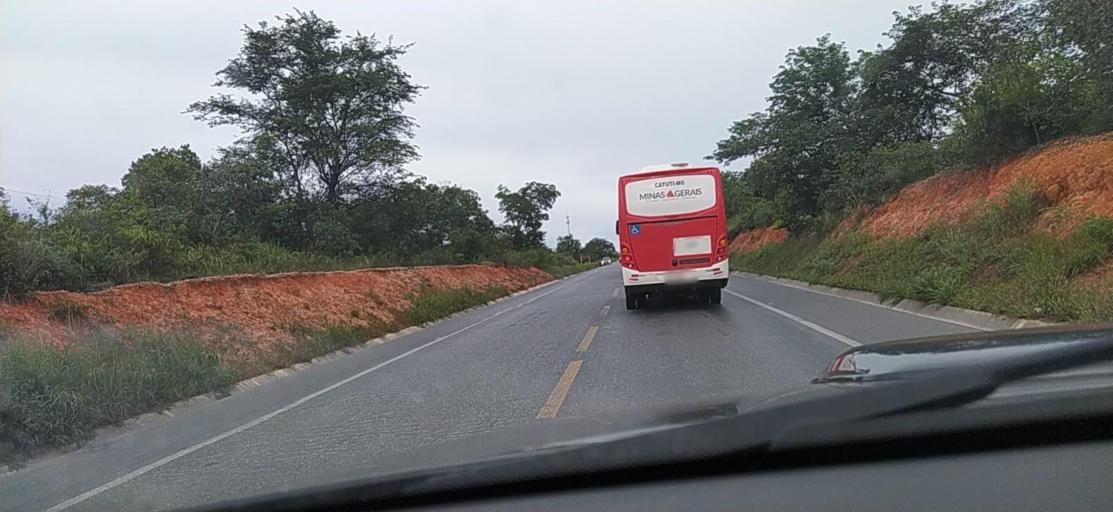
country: BR
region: Minas Gerais
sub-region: Montes Claros
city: Montes Claros
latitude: -16.6630
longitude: -43.7722
